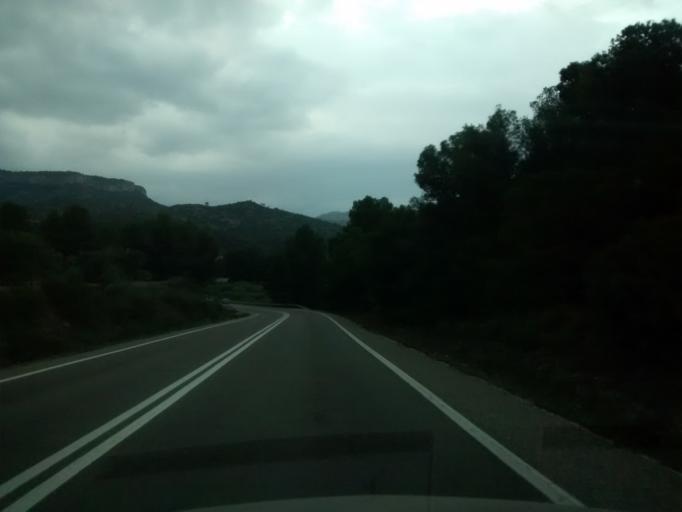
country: ES
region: Catalonia
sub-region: Provincia de Tarragona
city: Benifallet
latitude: 41.0207
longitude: 0.5005
